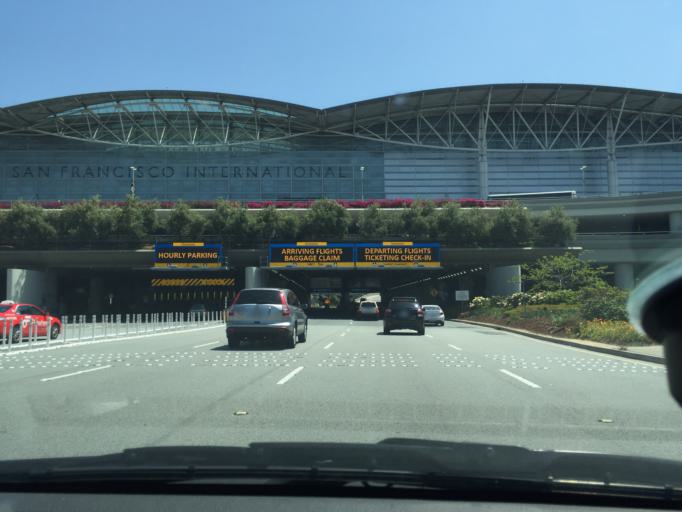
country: US
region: California
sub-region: San Mateo County
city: Millbrae
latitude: 37.6149
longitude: -122.3909
